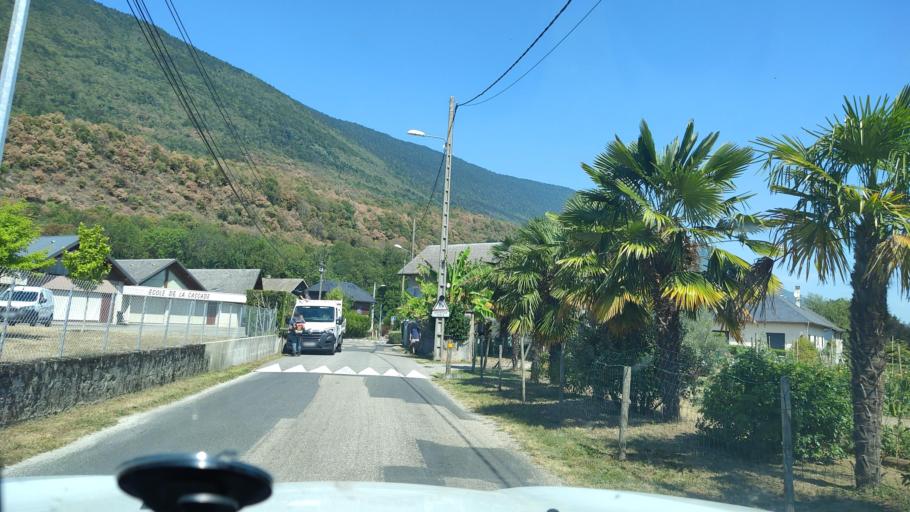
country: FR
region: Rhone-Alpes
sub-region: Departement de la Savoie
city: Le Bourget-du-Lac
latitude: 45.6240
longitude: 5.8495
